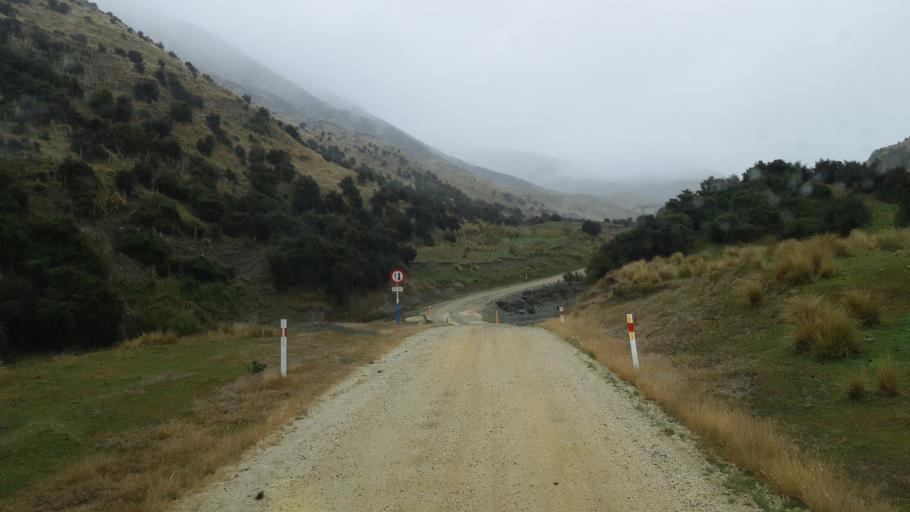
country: NZ
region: Otago
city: Oamaru
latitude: -44.9552
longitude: 170.4455
